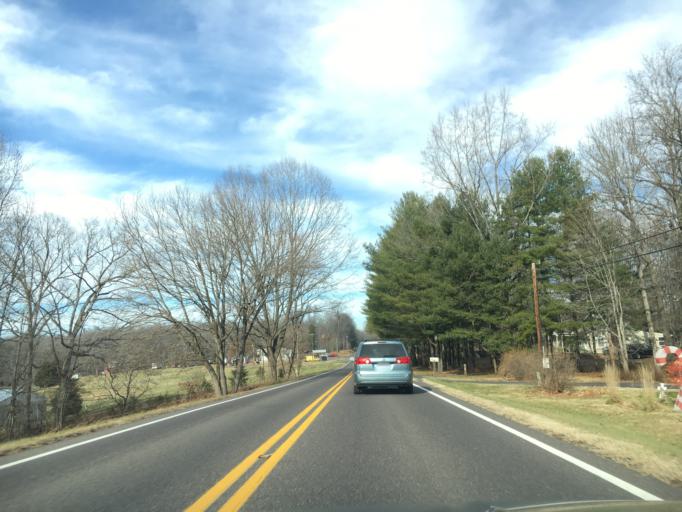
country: US
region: Virginia
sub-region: Culpeper County
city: Culpeper
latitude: 38.5586
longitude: -77.9807
